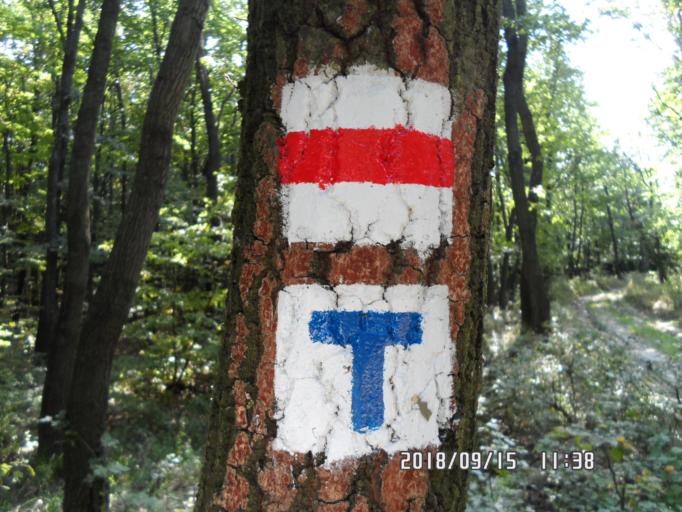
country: HU
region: Veszprem
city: Cseteny
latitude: 47.2585
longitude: 17.9799
